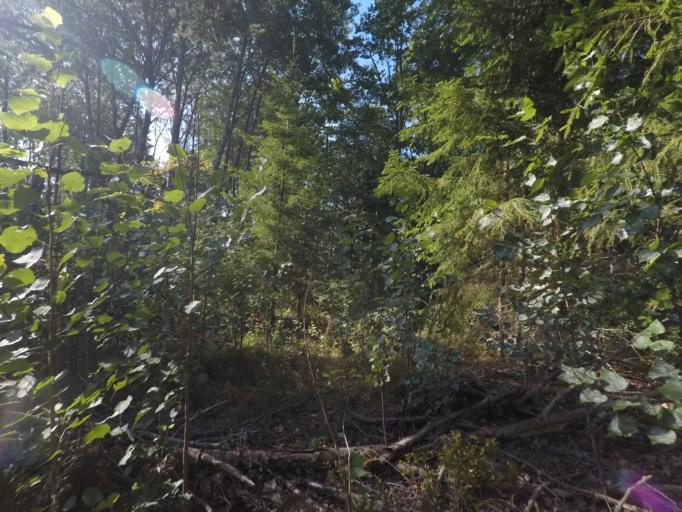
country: SE
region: Soedermanland
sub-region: Eskilstuna Kommun
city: Kvicksund
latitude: 59.4454
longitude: 16.2652
